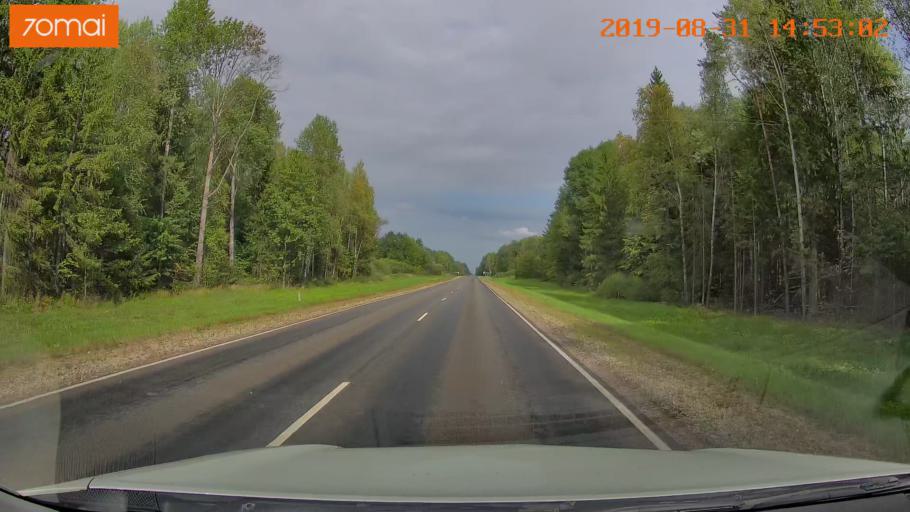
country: RU
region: Kaluga
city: Spas-Demensk
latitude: 54.2803
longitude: 33.8542
